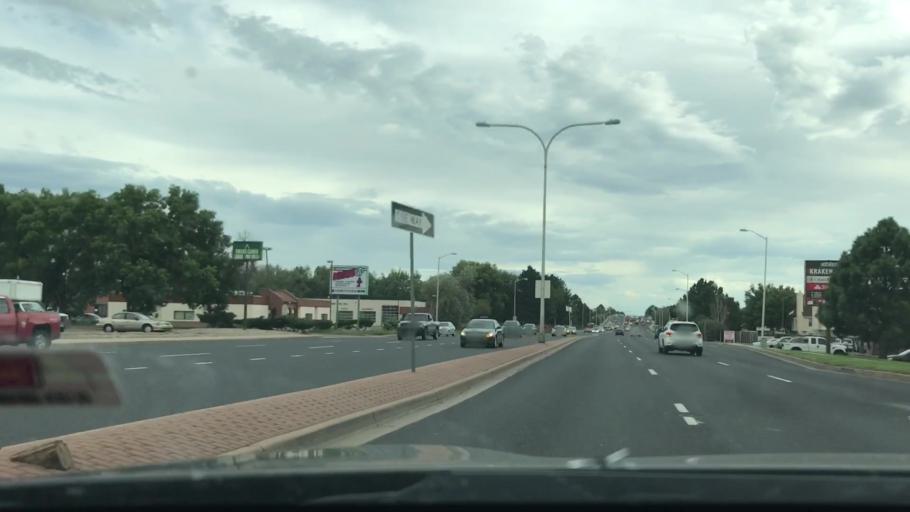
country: US
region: Colorado
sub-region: El Paso County
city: Cimarron Hills
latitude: 38.8890
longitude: -104.7570
